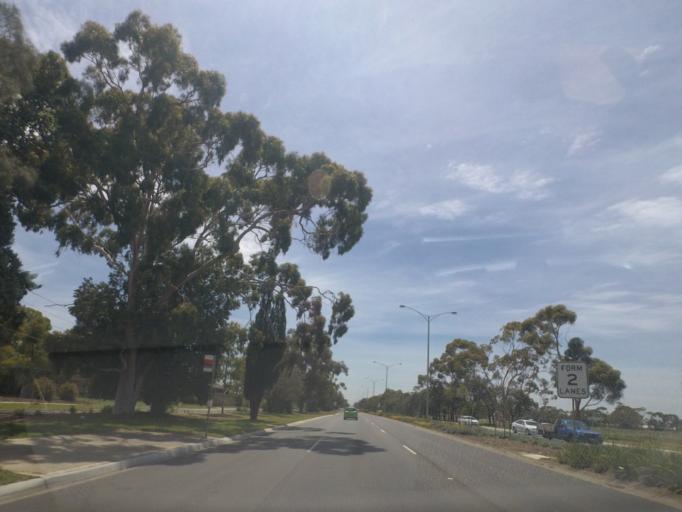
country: AU
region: Victoria
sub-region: Wyndham
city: Werribee
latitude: -37.8958
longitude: 144.6761
